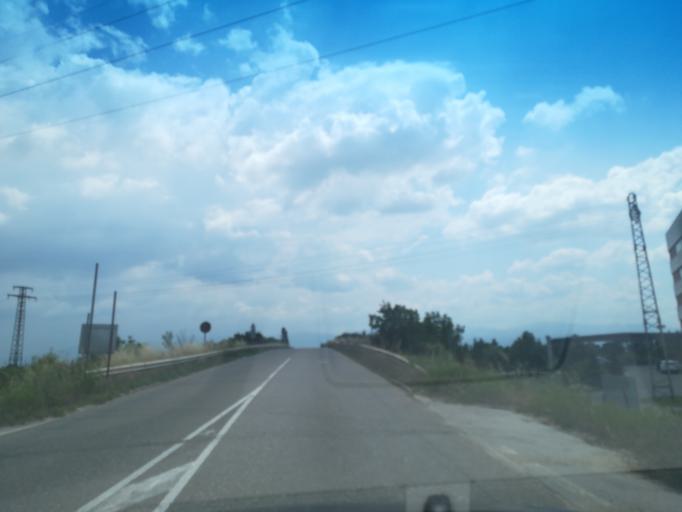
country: BG
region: Plovdiv
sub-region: Obshtina Plovdiv
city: Plovdiv
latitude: 42.1922
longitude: 24.6763
